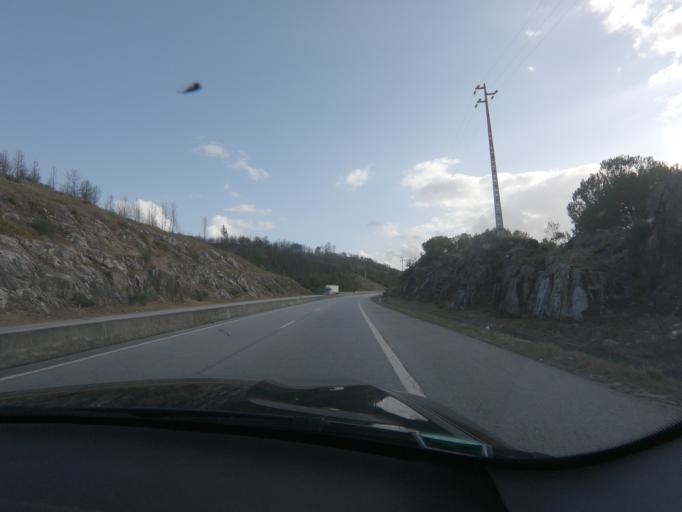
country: PT
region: Viseu
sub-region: Viseu
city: Viseu
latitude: 40.6095
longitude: -7.9679
